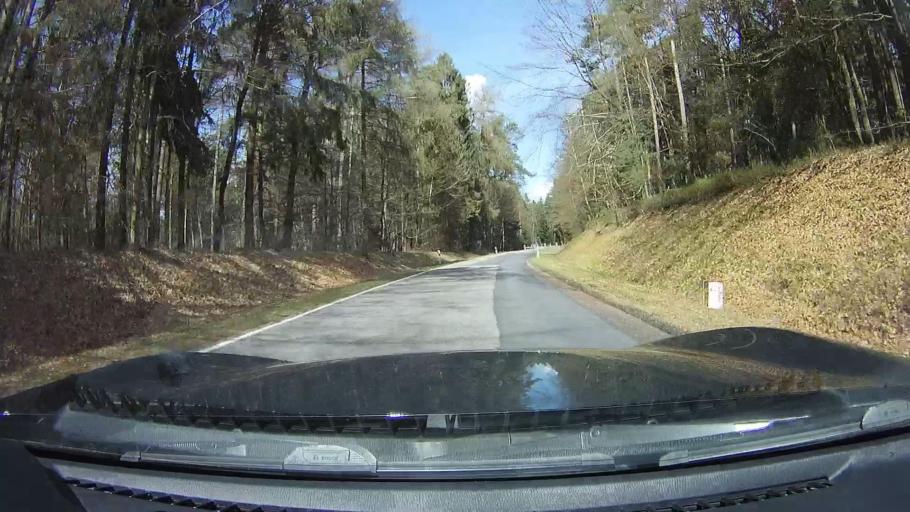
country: DE
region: Hesse
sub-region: Regierungsbezirk Darmstadt
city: Wald-Michelbach
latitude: 49.6017
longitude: 8.8991
